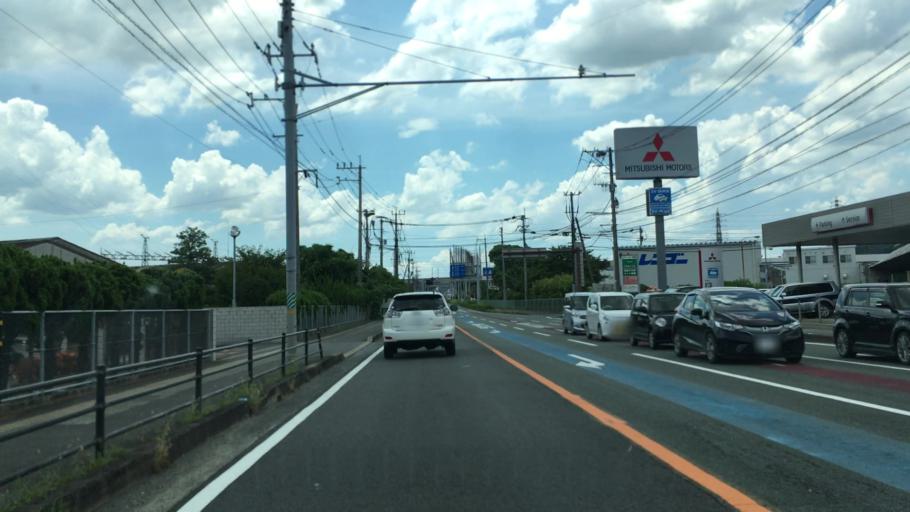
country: JP
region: Saga Prefecture
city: Tosu
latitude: 33.3648
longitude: 130.5018
